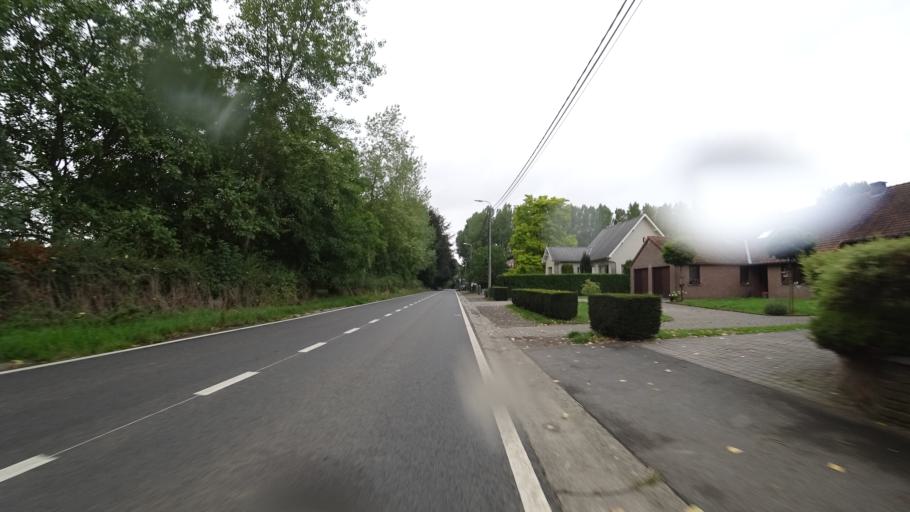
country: BE
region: Wallonia
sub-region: Province de Namur
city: Namur
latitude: 50.5307
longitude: 4.8452
